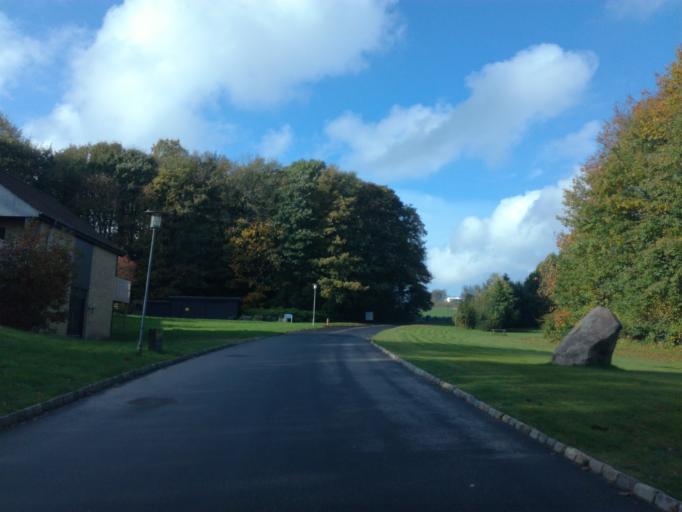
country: DK
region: South Denmark
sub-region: Vejle Kommune
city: Brejning
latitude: 55.6680
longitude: 9.6840
